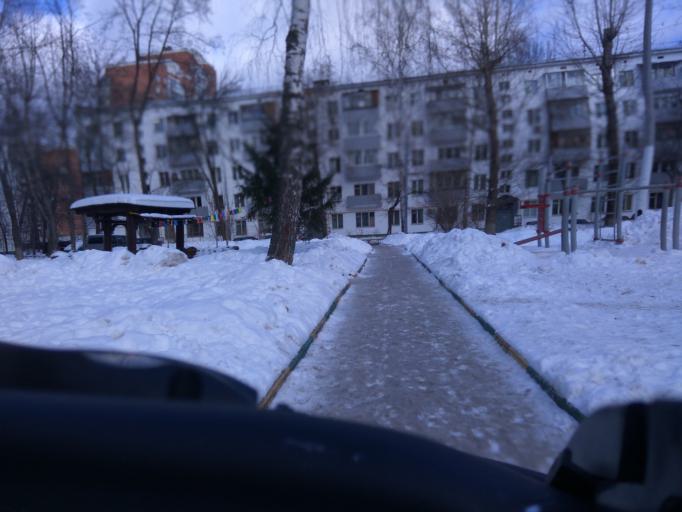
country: RU
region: Moskovskaya
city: Bogorodskoye
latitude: 55.7989
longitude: 37.7219
